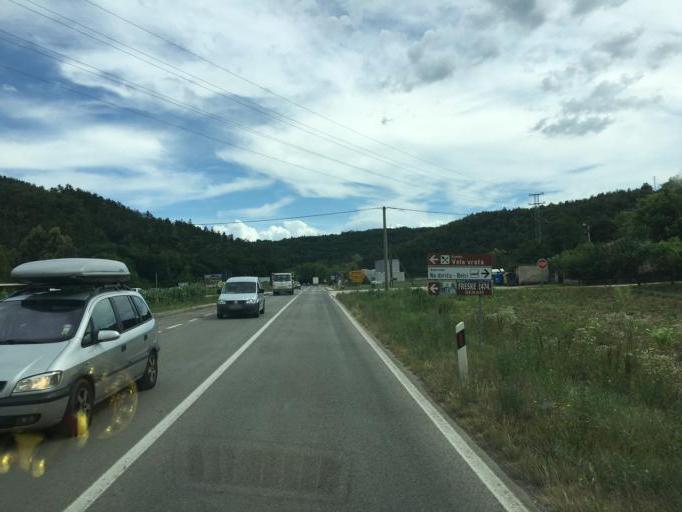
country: HR
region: Istarska
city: Pazin
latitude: 45.2524
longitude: 13.8943
